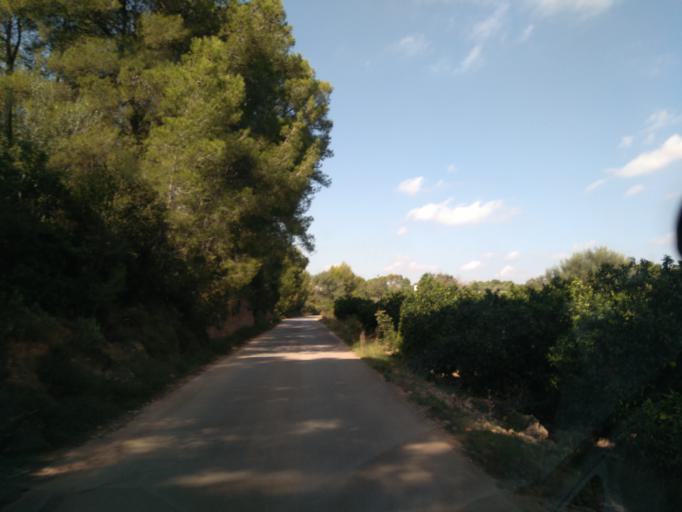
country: ES
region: Valencia
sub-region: Provincia de Valencia
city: Tous
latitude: 39.1770
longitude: -0.5976
